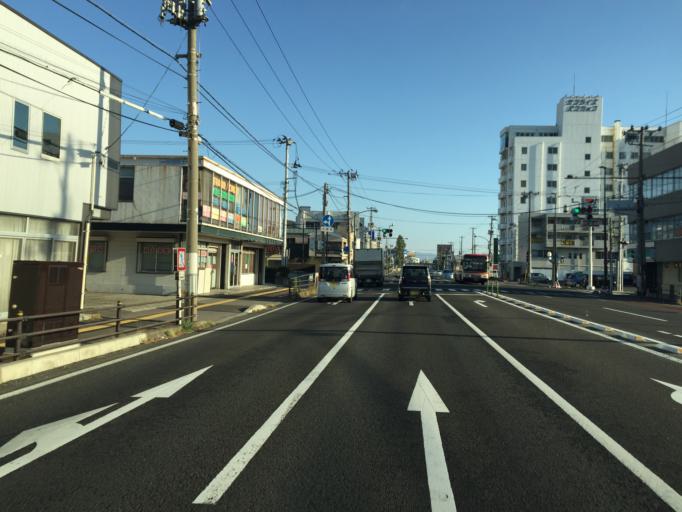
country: JP
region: Fukushima
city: Fukushima-shi
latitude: 37.7628
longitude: 140.4770
